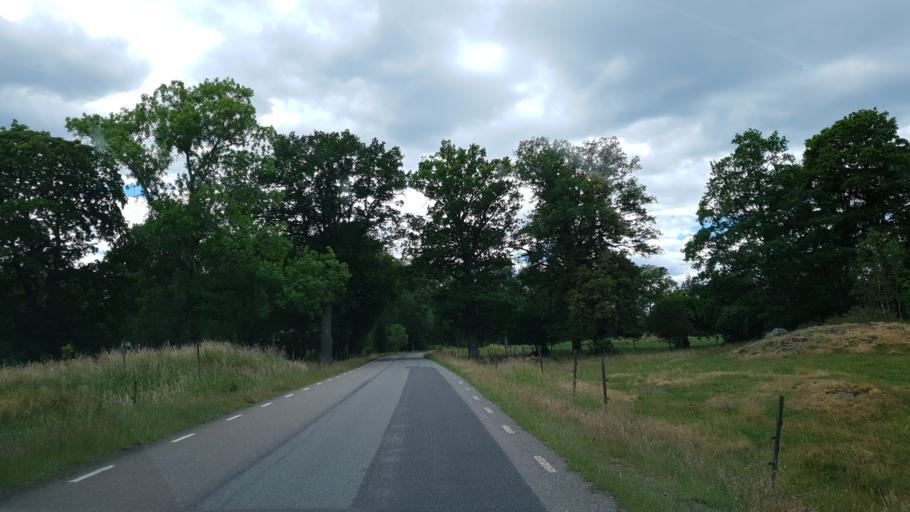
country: SE
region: Kalmar
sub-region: Hultsfreds Kommun
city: Virserum
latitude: 57.0605
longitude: 15.5945
